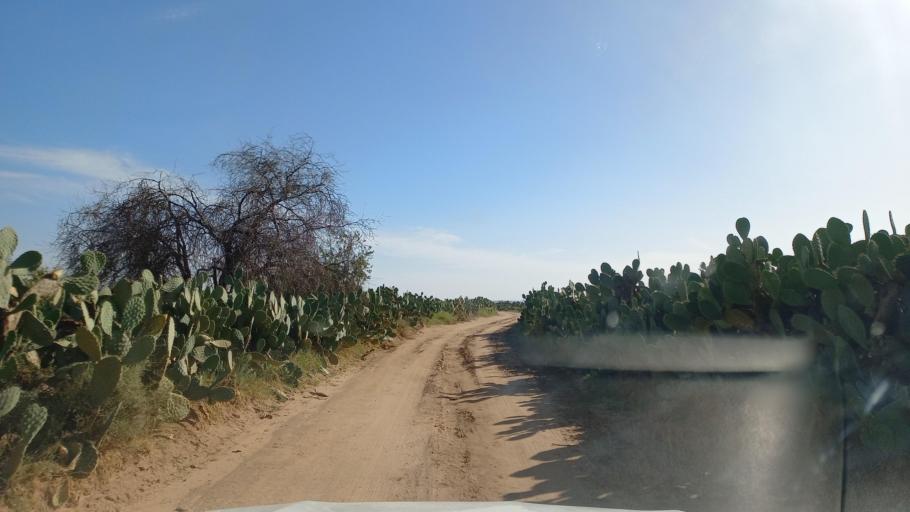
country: TN
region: Al Qasrayn
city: Sbiba
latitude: 35.3321
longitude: 9.1249
